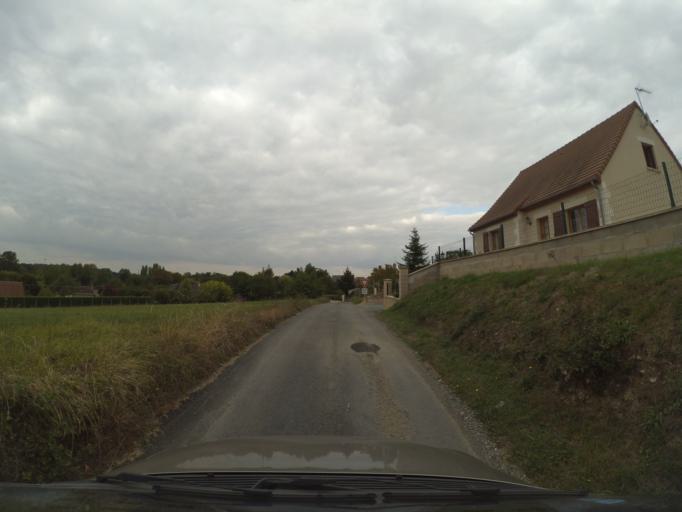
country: FR
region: Centre
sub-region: Departement d'Indre-et-Loire
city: Auzouer-en-Touraine
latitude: 47.5098
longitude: 0.9183
